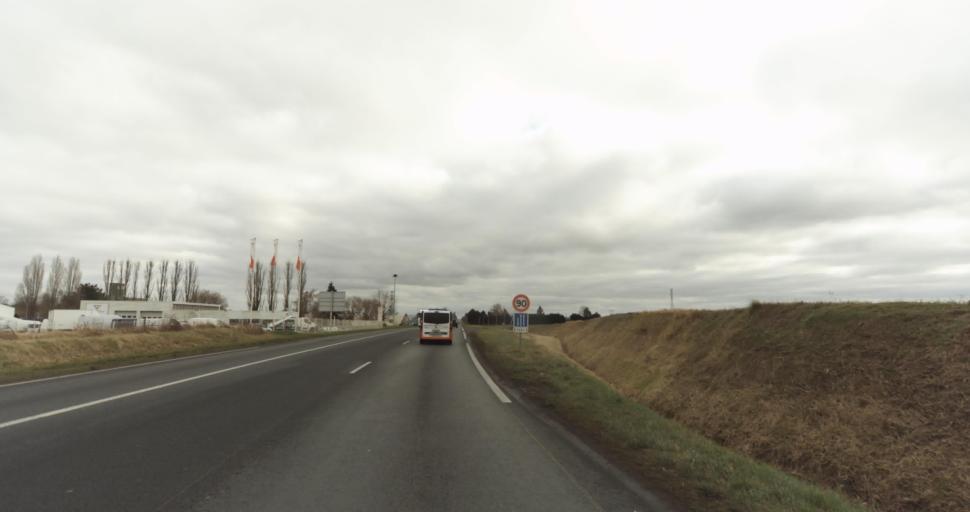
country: FR
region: Pays de la Loire
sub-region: Departement de Maine-et-Loire
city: Saint-Philbert-du-Peuple
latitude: 47.3694
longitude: -0.0977
